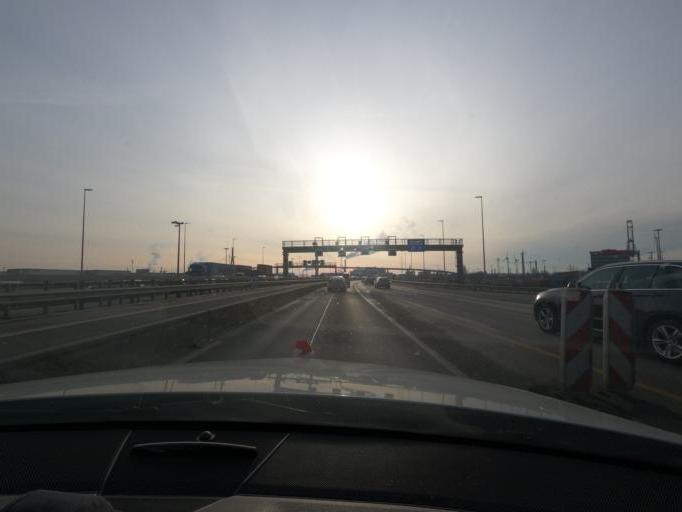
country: DE
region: Hamburg
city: Altona
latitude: 53.5320
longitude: 9.9333
